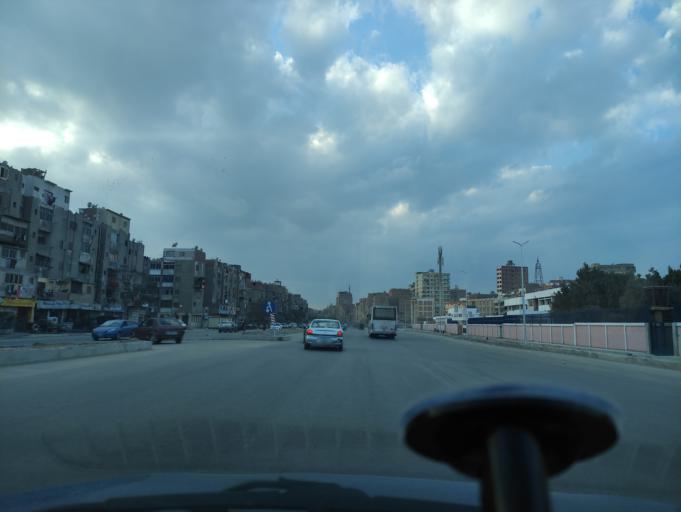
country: EG
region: Muhafazat al Qalyubiyah
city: Al Khankah
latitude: 30.1353
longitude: 31.3543
